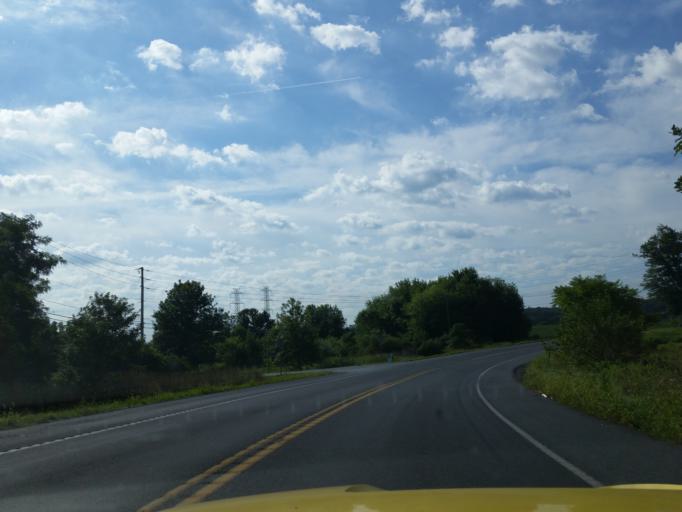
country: US
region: Pennsylvania
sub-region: Lebanon County
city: Sand Hill
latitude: 40.3857
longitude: -76.4113
